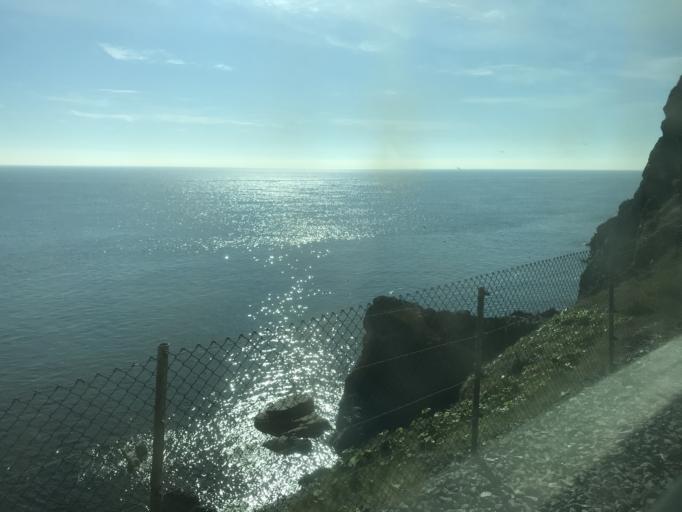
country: IE
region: Leinster
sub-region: Wicklow
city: Bray
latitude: 53.1907
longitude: -6.0789
